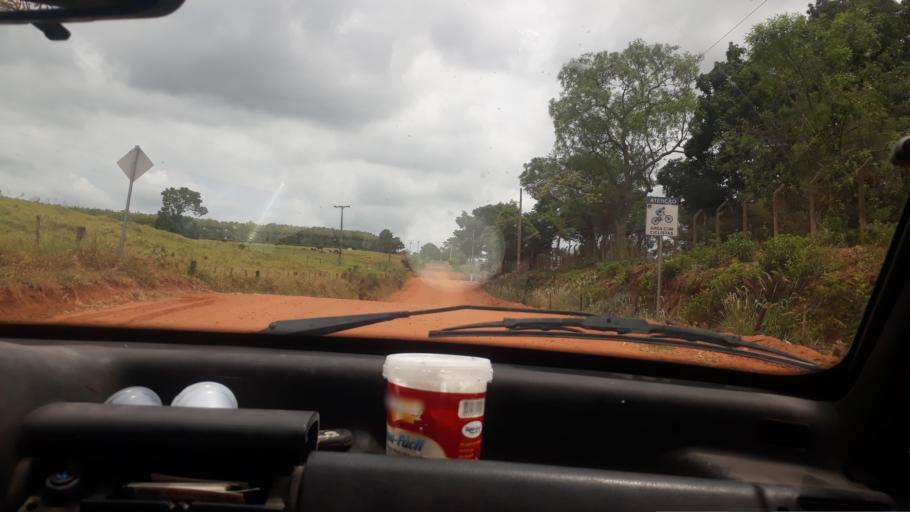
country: BR
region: Sao Paulo
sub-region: Regente Feijo
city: Regente Feijo
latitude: -22.2369
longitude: -51.2982
